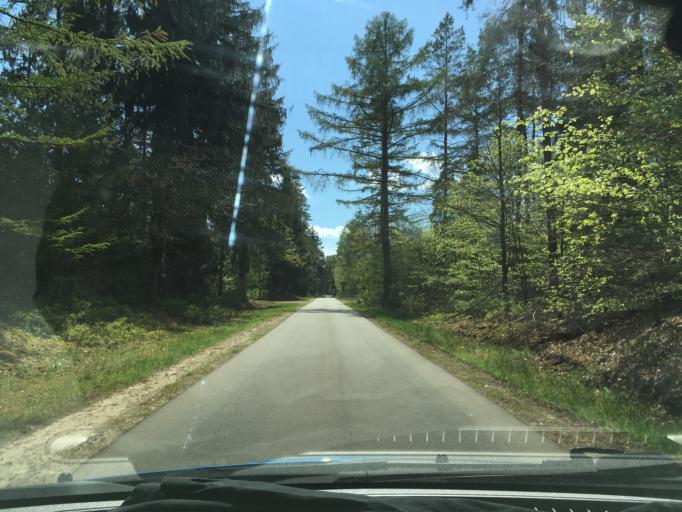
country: DE
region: Lower Saxony
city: Stoetze
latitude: 53.1096
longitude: 10.7857
